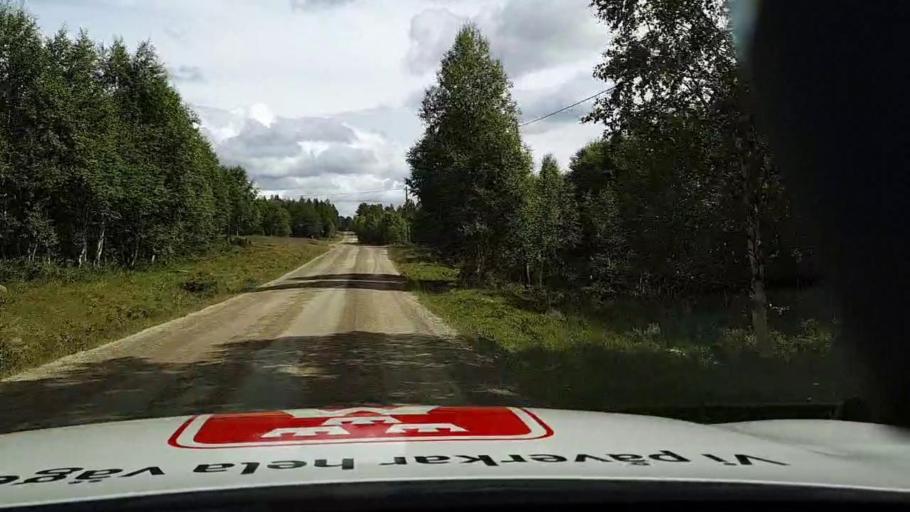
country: SE
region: Jaemtland
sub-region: Are Kommun
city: Jarpen
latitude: 62.5519
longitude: 13.4439
